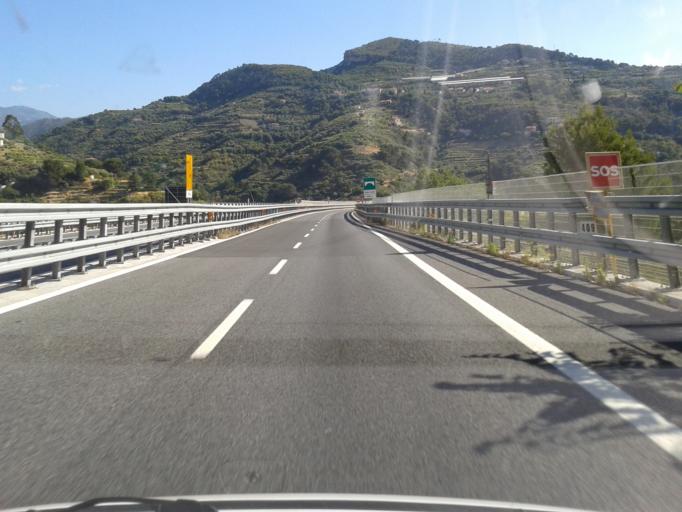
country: IT
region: Liguria
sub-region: Provincia di Imperia
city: Ventimiglia
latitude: 43.7960
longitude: 7.5593
